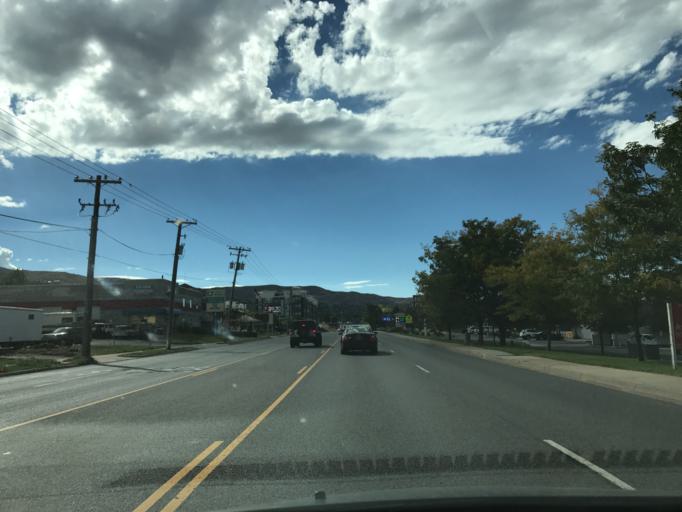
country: US
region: Utah
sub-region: Davis County
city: Woods Cross
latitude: 40.8736
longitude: -111.8923
